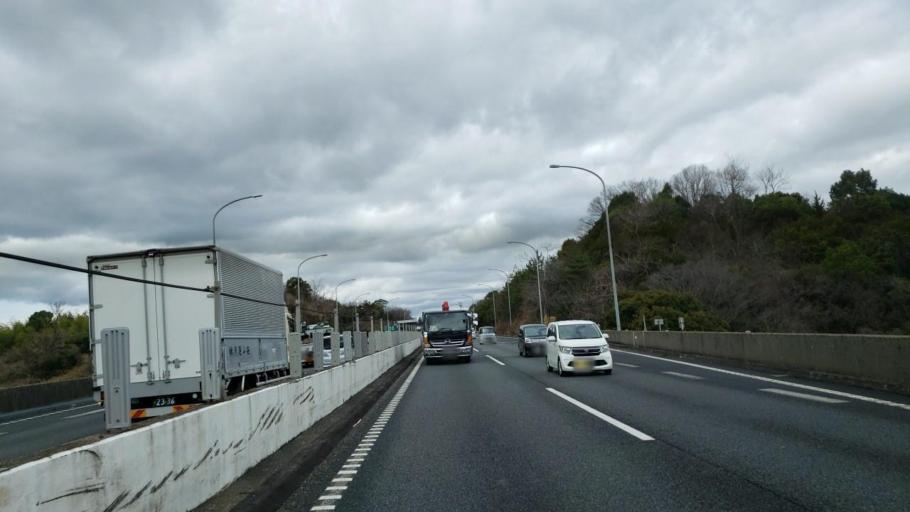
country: JP
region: Hyogo
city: Akashi
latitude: 34.7031
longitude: 134.9599
